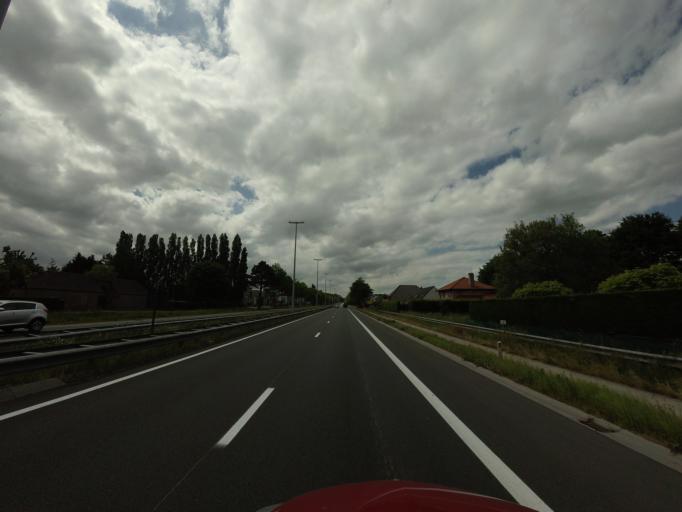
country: BE
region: Flanders
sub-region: Provincie Oost-Vlaanderen
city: Maldegem
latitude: 51.1806
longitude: 3.4490
